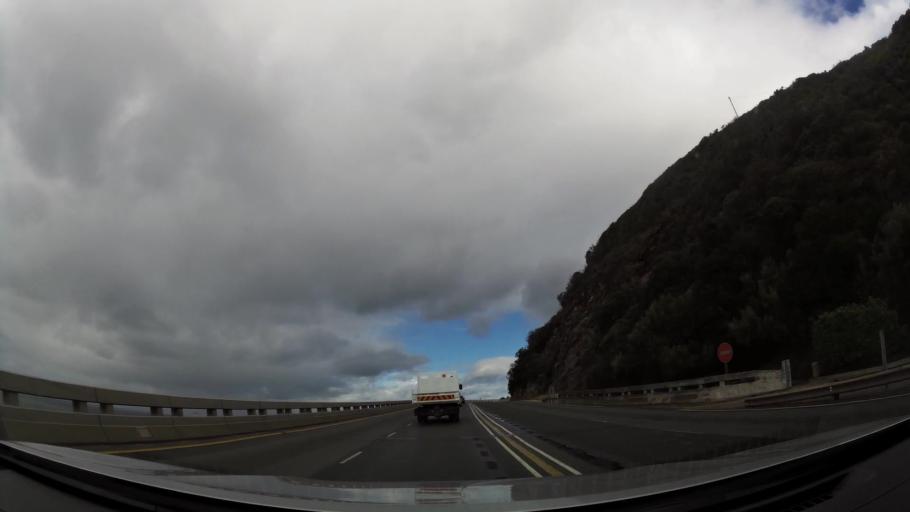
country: ZA
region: Western Cape
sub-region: Eden District Municipality
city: George
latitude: -33.9966
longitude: 22.5617
